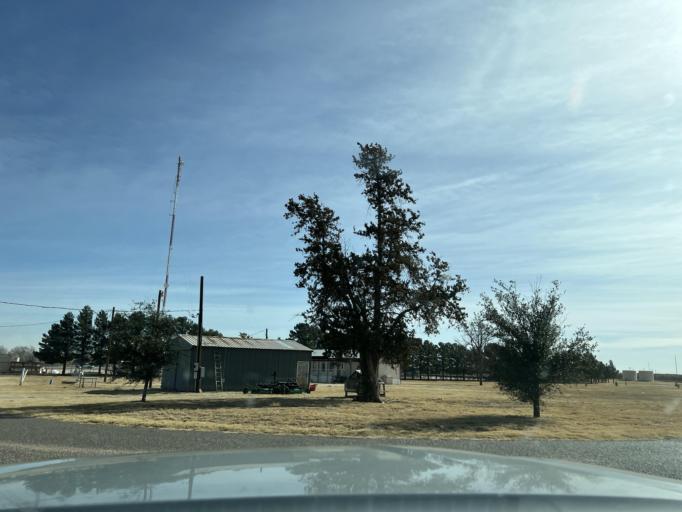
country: US
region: Texas
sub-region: Andrews County
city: Andrews
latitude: 32.4566
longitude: -102.5707
